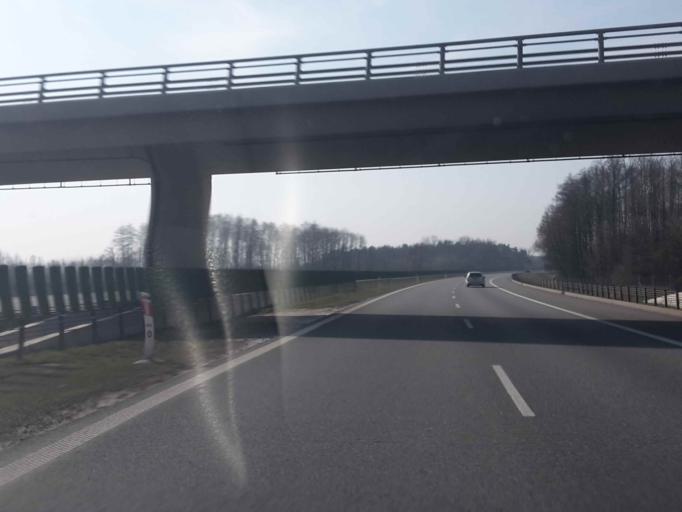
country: PL
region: Kujawsko-Pomorskie
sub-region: Powiat torunski
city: Lubicz Dolny
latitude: 52.9825
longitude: 18.7329
